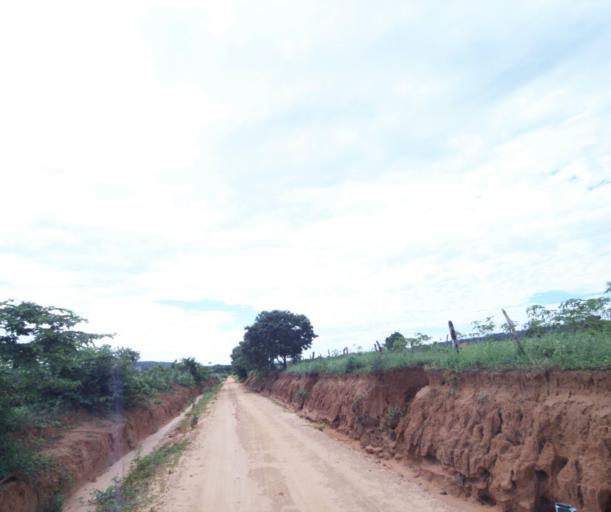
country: BR
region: Bahia
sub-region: Carinhanha
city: Carinhanha
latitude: -14.2084
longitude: -44.4584
